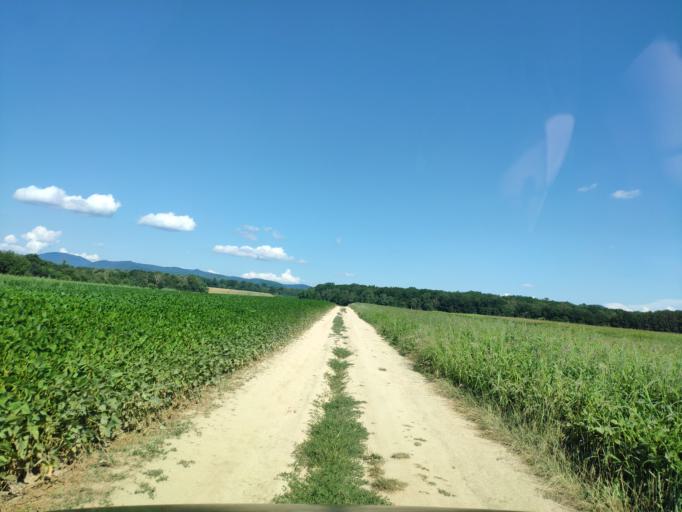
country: SK
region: Presovsky
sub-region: Okres Presov
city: Presov
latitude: 48.9062
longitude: 21.2800
